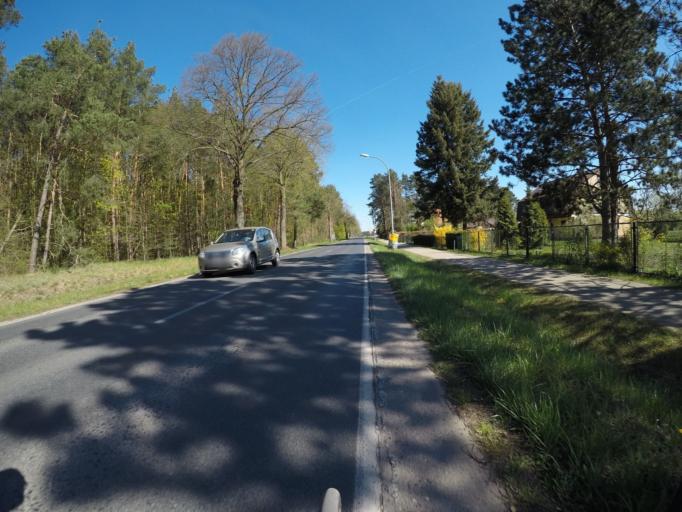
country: DE
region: Brandenburg
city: Strausberg
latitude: 52.5711
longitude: 13.9039
